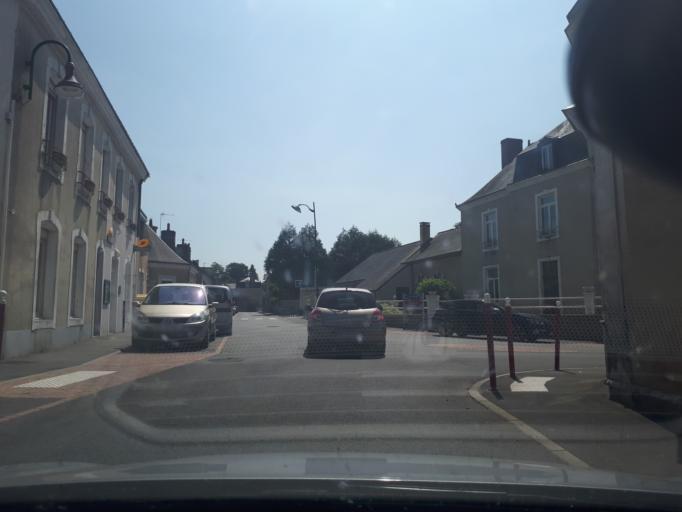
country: FR
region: Pays de la Loire
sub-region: Departement de la Sarthe
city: Le Breil-sur-Merize
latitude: 48.0093
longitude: 0.4760
